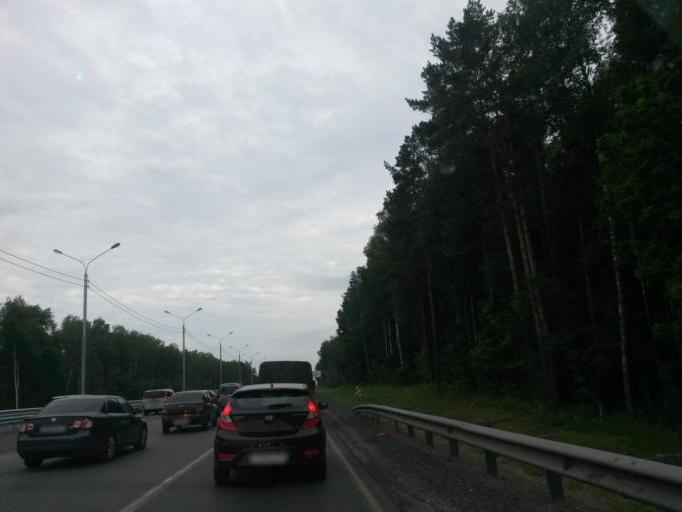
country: RU
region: Moskovskaya
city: Lyubuchany
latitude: 55.2649
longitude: 37.5350
